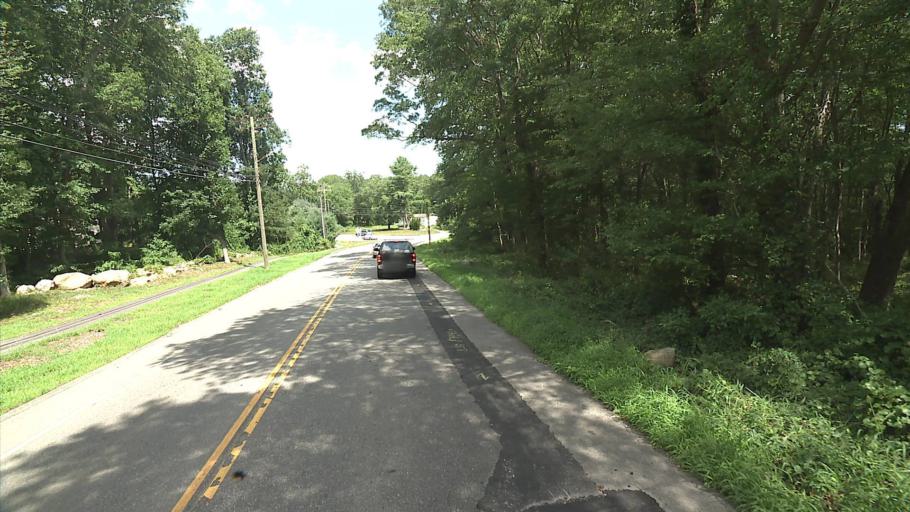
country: US
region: Connecticut
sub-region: New London County
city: Poquonock Bridge
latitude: 41.3504
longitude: -72.0097
